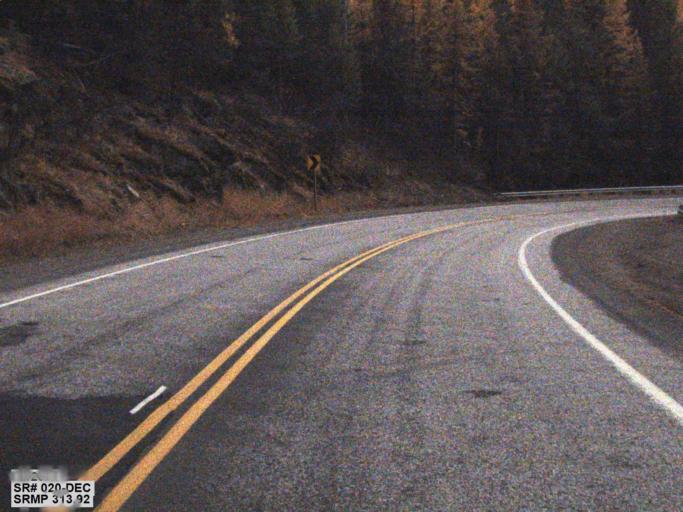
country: US
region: Washington
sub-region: Ferry County
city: Republic
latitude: 48.6127
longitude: -118.5647
